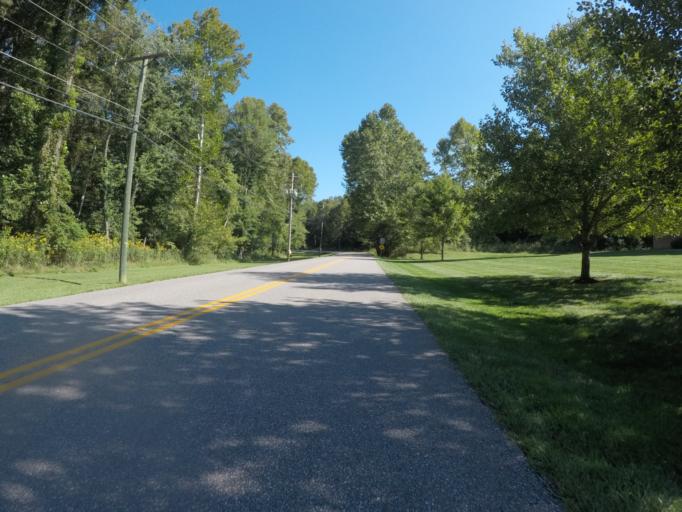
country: US
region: Kentucky
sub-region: Greenup County
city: Russell
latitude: 38.5108
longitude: -82.6943
